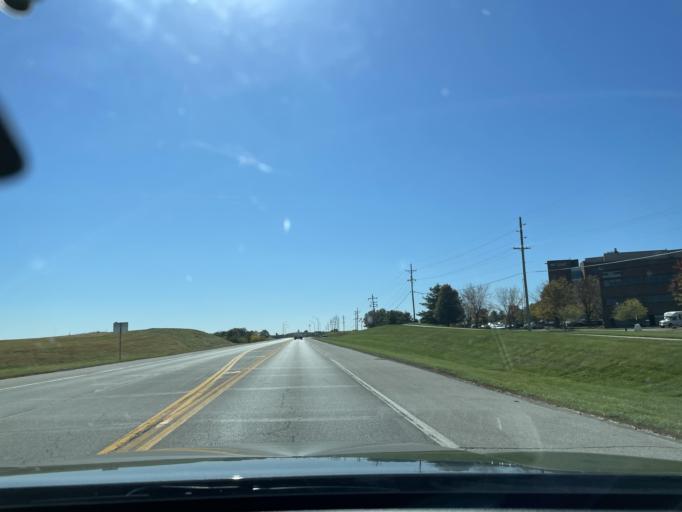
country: US
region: Missouri
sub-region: Buchanan County
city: Saint Joseph
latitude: 39.7741
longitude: -94.7679
